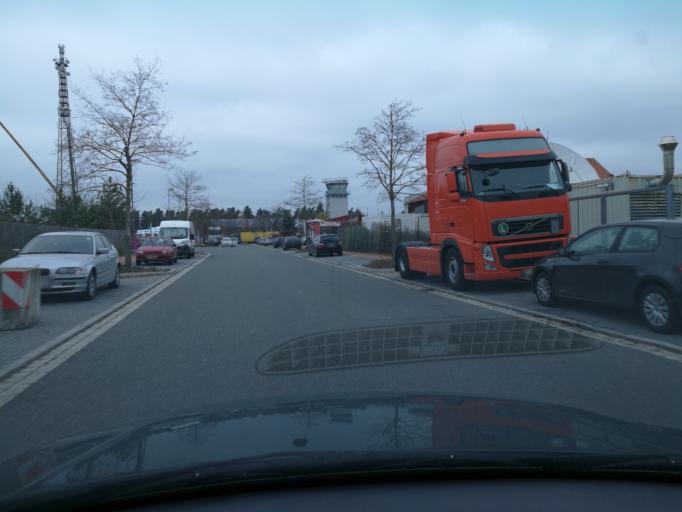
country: DE
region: Bavaria
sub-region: Regierungsbezirk Mittelfranken
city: Feucht
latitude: 49.3875
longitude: 11.1781
